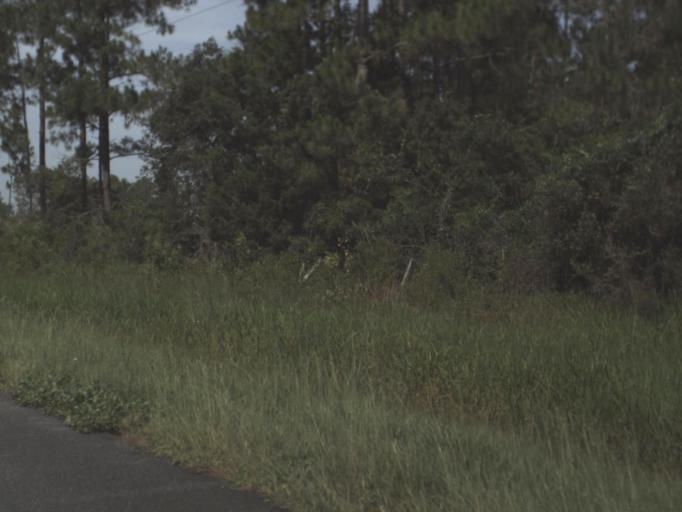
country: US
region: Florida
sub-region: Lafayette County
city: Mayo
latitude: 30.0280
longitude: -83.1867
